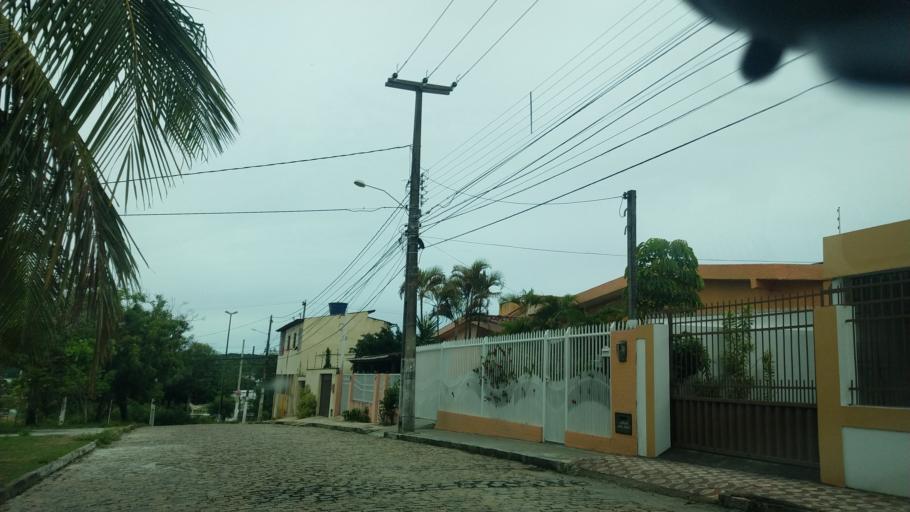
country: BR
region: Rio Grande do Norte
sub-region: Natal
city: Natal
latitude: -5.8408
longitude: -35.2081
